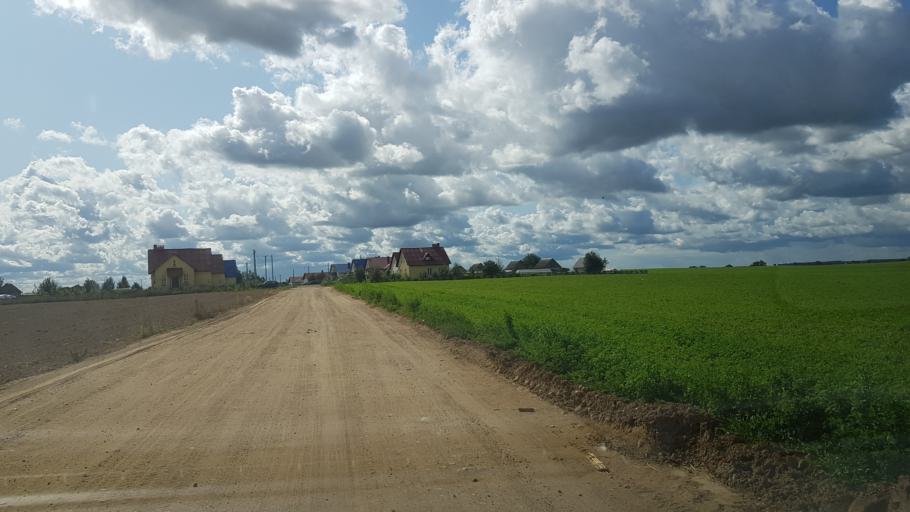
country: BY
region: Minsk
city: Dzyarzhynsk
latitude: 53.7478
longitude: 27.2125
